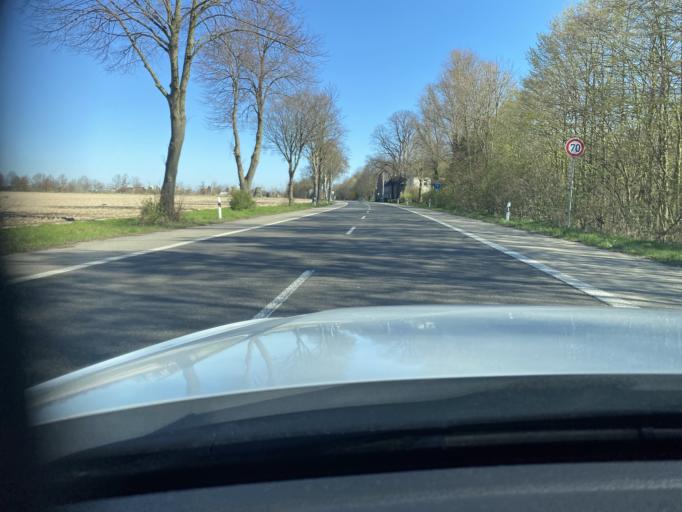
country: DE
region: North Rhine-Westphalia
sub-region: Regierungsbezirk Dusseldorf
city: Neubrueck
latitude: 51.1460
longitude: 6.6543
